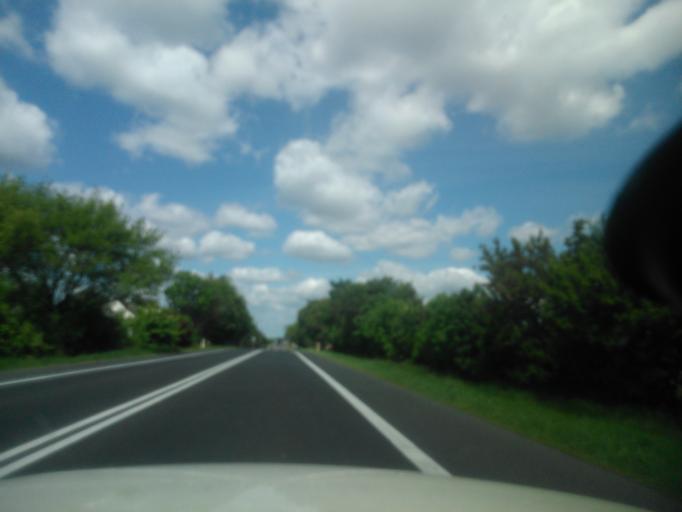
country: PL
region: Kujawsko-Pomorskie
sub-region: Powiat torunski
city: Lubicz Gorny
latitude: 53.0123
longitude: 18.8247
